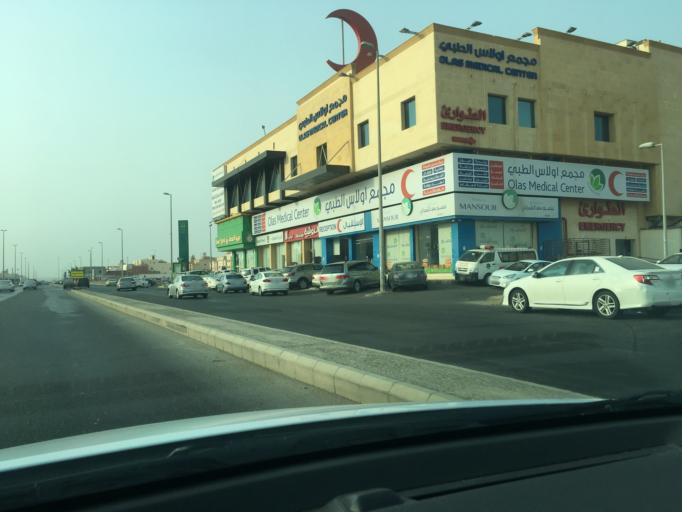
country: SA
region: Makkah
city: Jeddah
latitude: 21.7561
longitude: 39.1857
